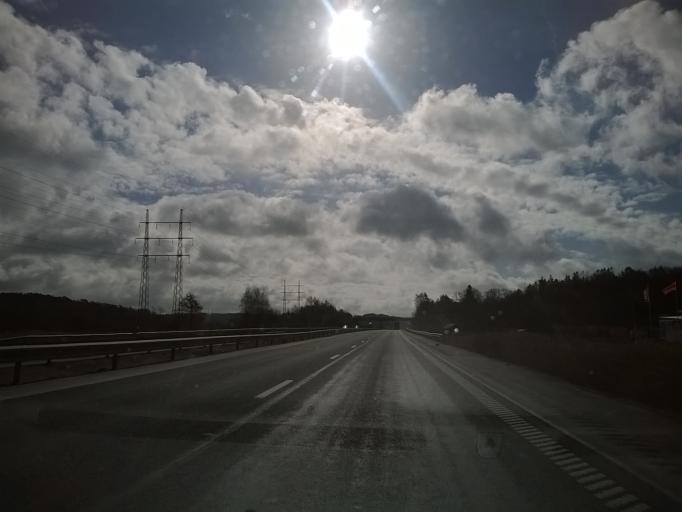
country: SE
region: Halland
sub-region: Kungsbacka Kommun
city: Kungsbacka
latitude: 57.4660
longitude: 12.0712
